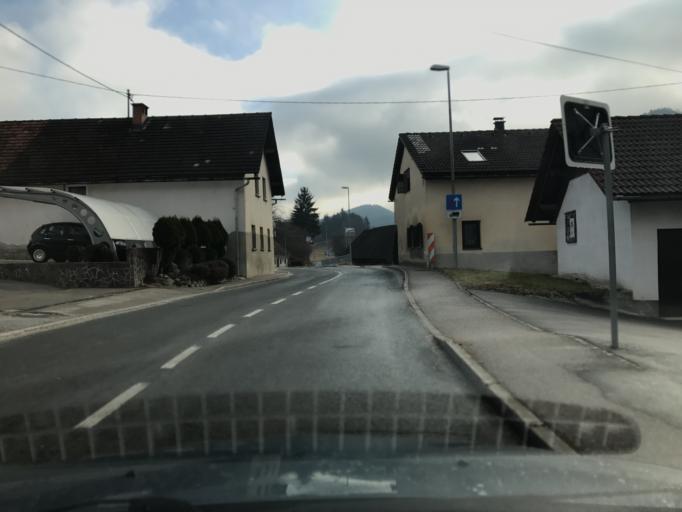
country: SI
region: Lukovica
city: Lukovica pri Domzalah
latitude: 46.2163
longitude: 14.7217
